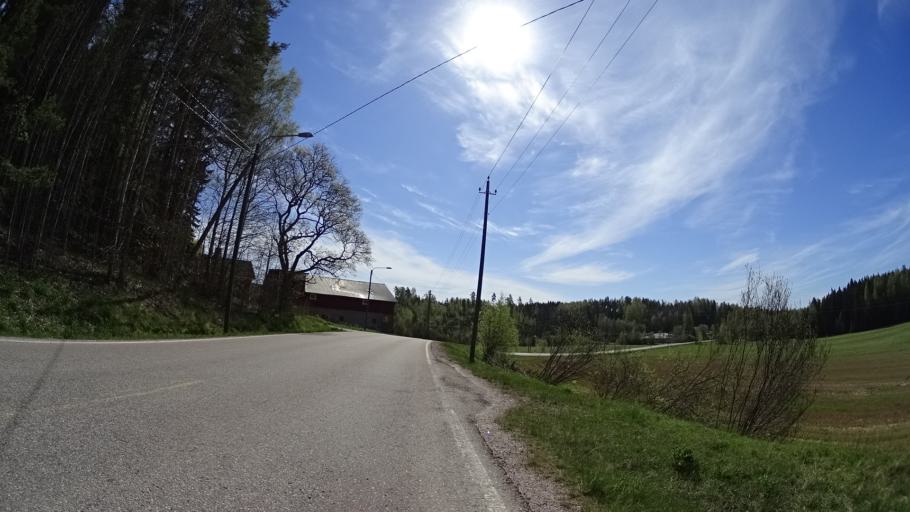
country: FI
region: Uusimaa
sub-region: Helsinki
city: Nurmijaervi
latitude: 60.3813
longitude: 24.8375
